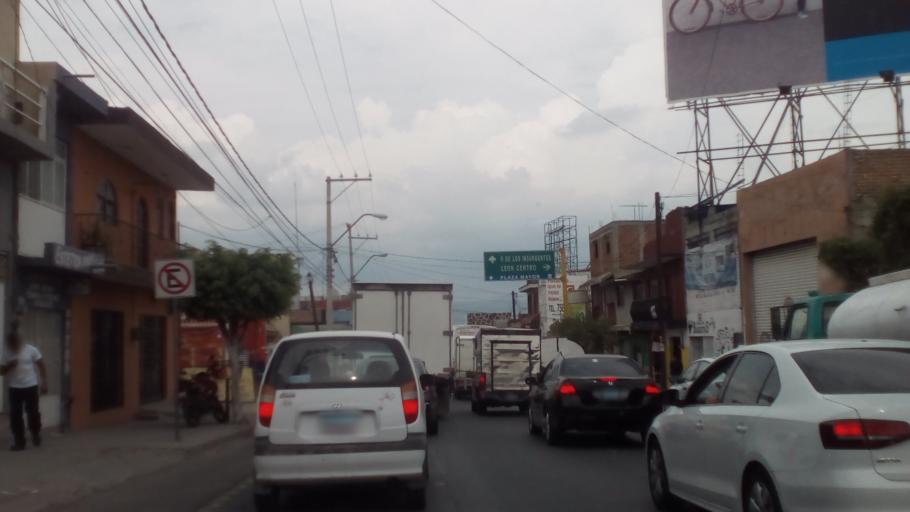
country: MX
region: Guanajuato
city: Leon
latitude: 21.1293
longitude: -101.7040
